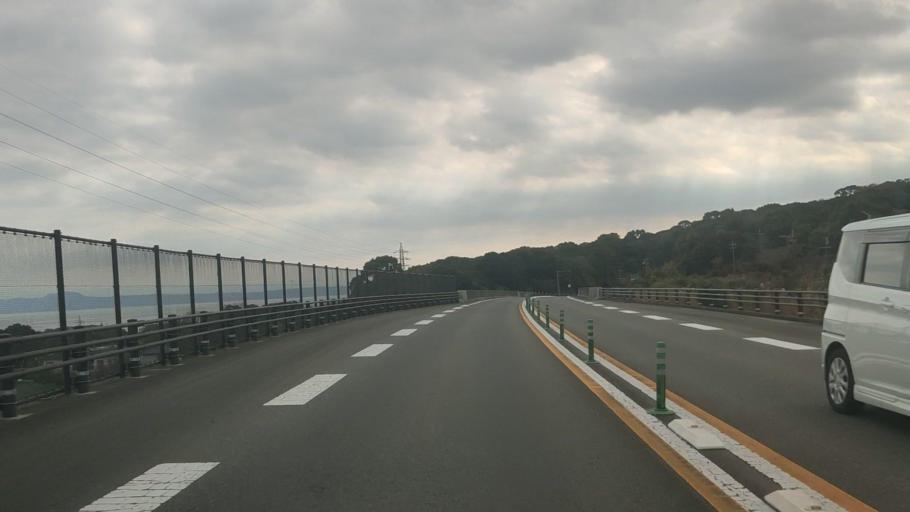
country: JP
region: Nagasaki
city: Shimabara
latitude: 32.7818
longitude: 130.3545
